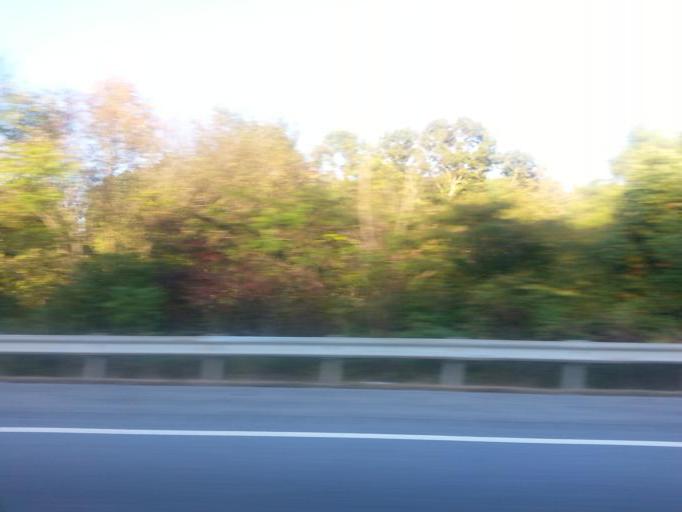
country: US
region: Tennessee
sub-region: Anderson County
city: Norris
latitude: 36.1785
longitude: -84.0916
